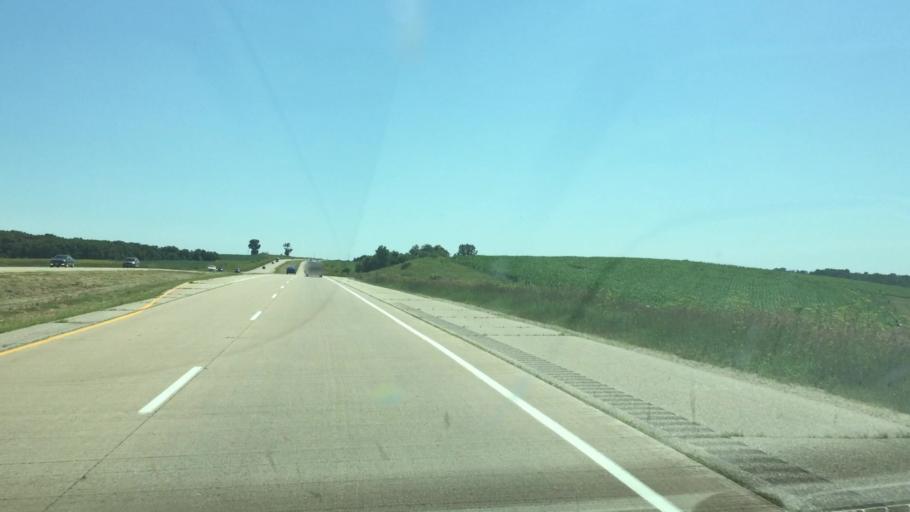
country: US
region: Wisconsin
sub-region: Iowa County
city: Mineral Point
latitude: 42.8056
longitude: -90.2718
